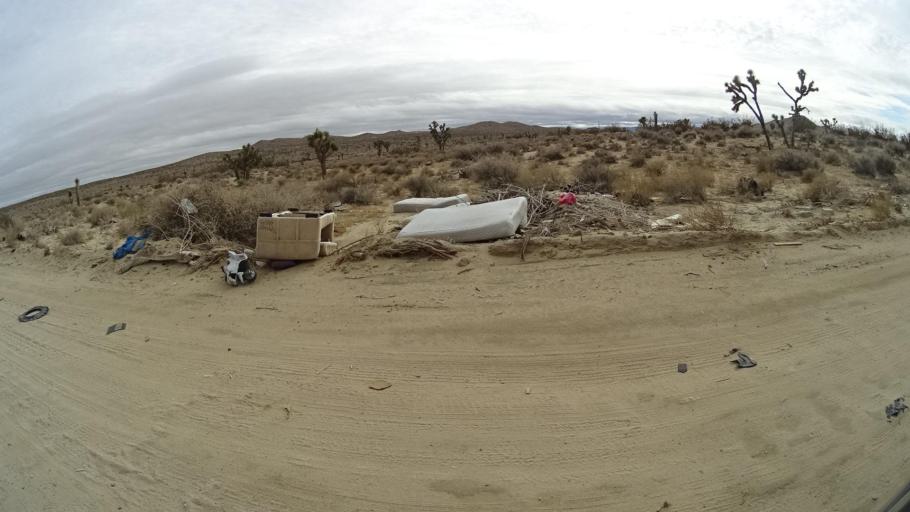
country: US
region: California
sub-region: Kern County
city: Rosamond
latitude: 34.9082
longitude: -118.1552
